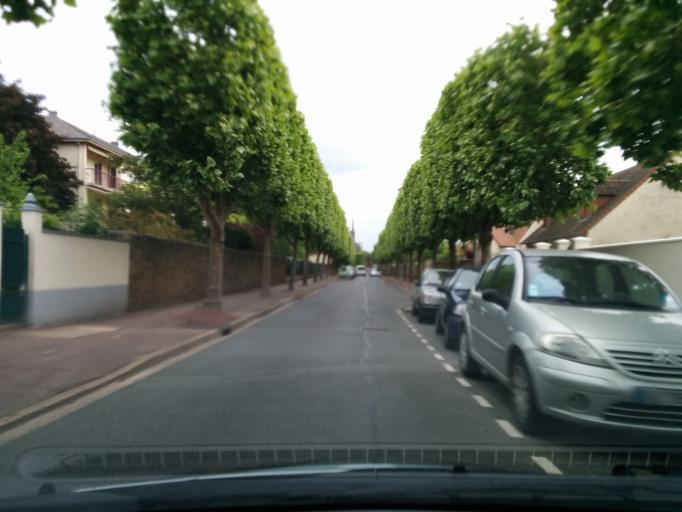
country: FR
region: Ile-de-France
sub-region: Departement des Yvelines
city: Juziers
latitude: 48.9744
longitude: 1.8404
